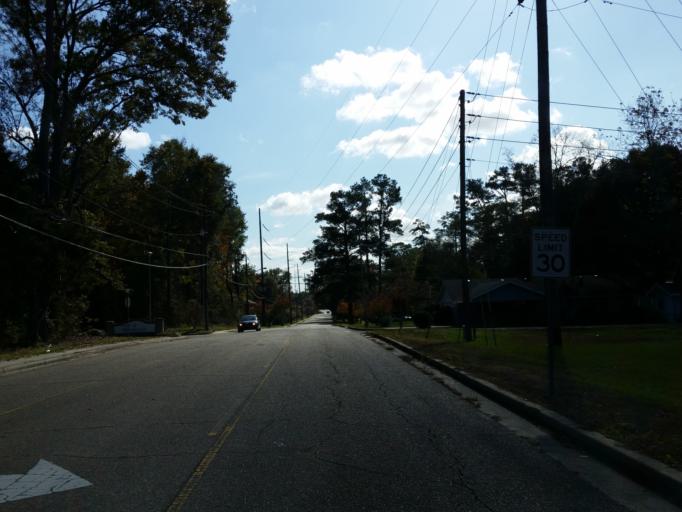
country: US
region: Mississippi
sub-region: Forrest County
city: Hattiesburg
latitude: 31.3097
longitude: -89.3312
